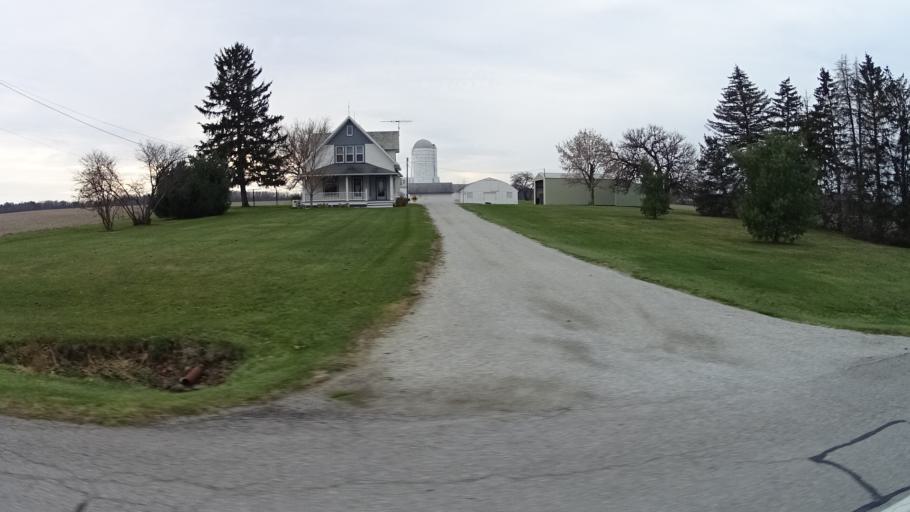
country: US
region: Ohio
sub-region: Lorain County
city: Lagrange
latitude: 41.1683
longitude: -82.0860
